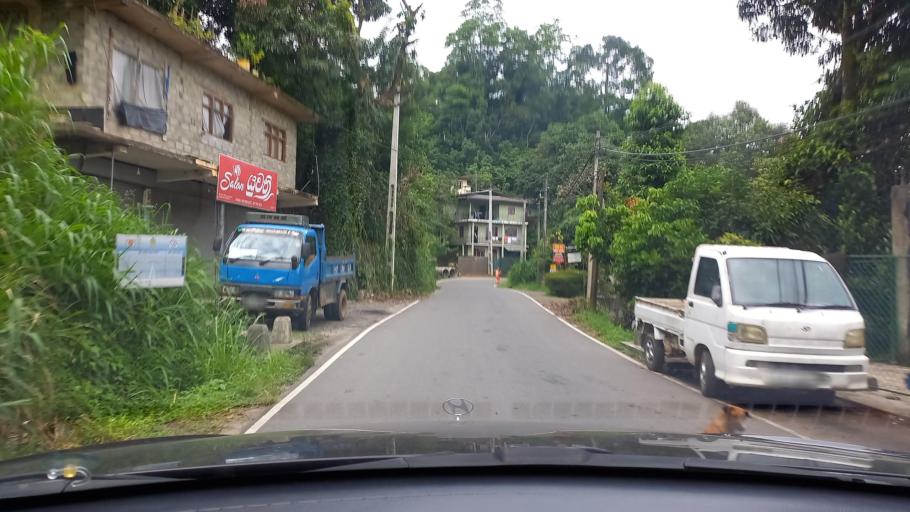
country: LK
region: Central
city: Kandy
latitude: 7.2294
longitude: 80.6060
